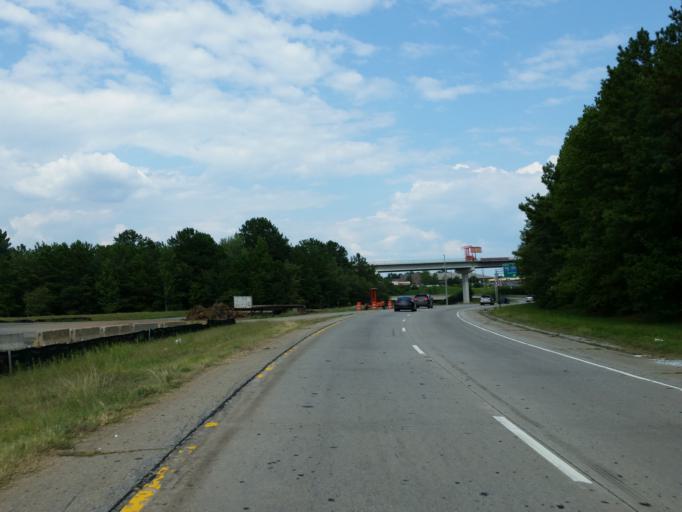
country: US
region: Georgia
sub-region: Cobb County
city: Marietta
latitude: 33.9820
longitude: -84.5440
